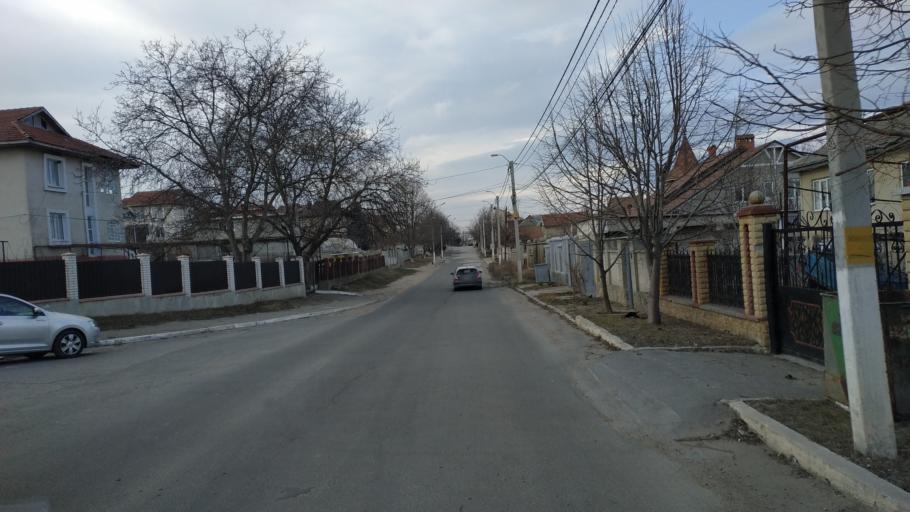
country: MD
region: Laloveni
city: Ialoveni
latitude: 46.9590
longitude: 28.7576
